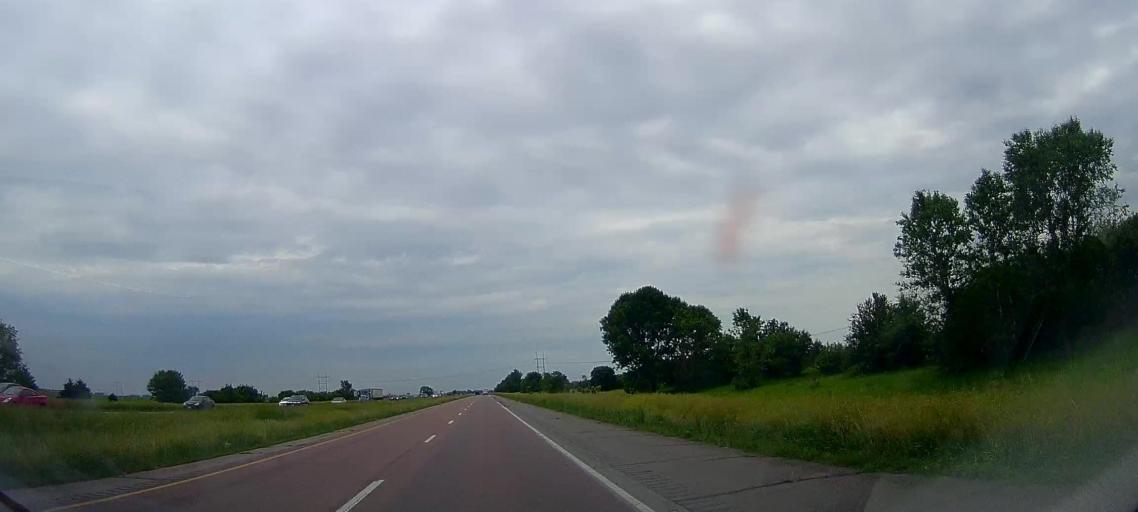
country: US
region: Iowa
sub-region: Woodbury County
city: Sergeant Bluff
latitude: 42.3633
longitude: -96.3450
